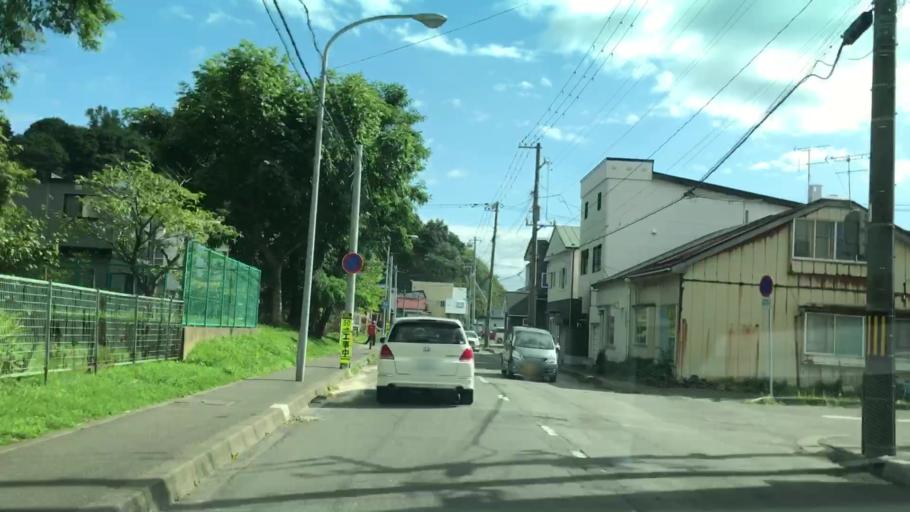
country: JP
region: Hokkaido
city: Muroran
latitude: 42.3136
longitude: 140.9735
